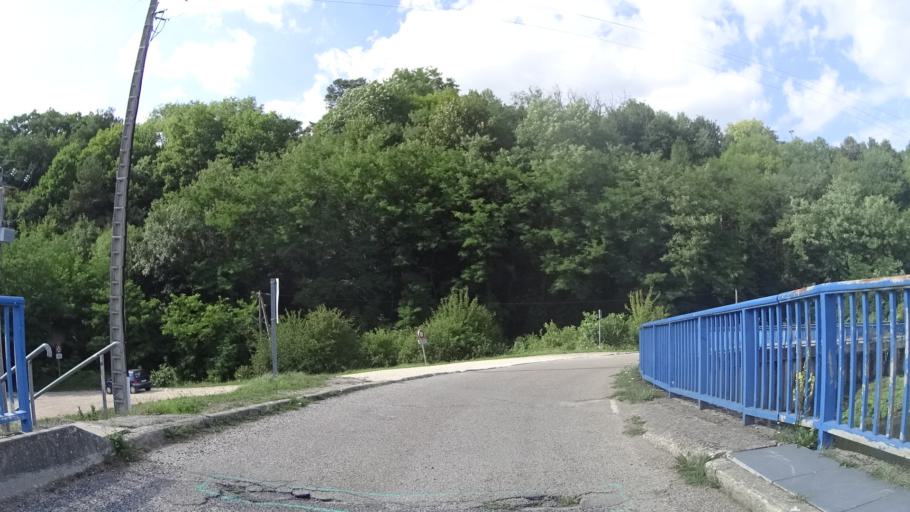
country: FR
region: Lorraine
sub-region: Departement de Meurthe-et-Moselle
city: Gondreville
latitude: 48.6518
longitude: 5.9780
